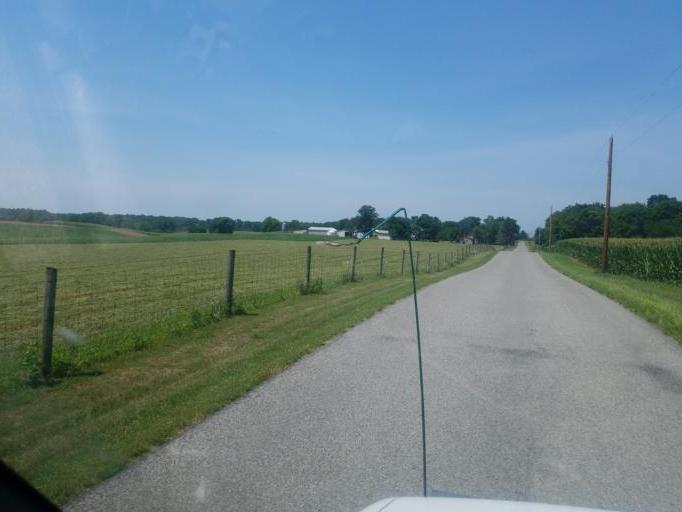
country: US
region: Ohio
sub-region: Logan County
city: West Liberty
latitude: 40.2909
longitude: -83.8097
